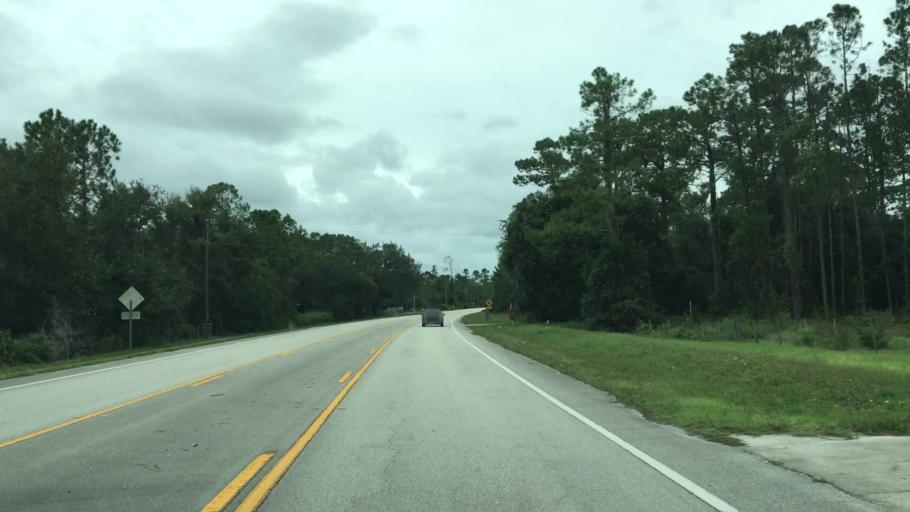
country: US
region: Florida
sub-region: Volusia County
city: Lake Helen
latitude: 28.9898
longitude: -81.2236
